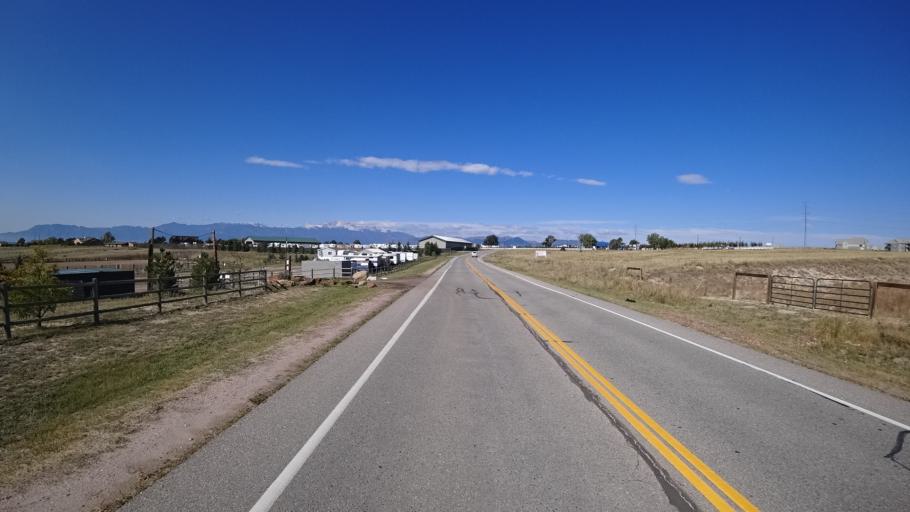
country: US
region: Colorado
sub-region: El Paso County
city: Black Forest
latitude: 38.9390
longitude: -104.7038
